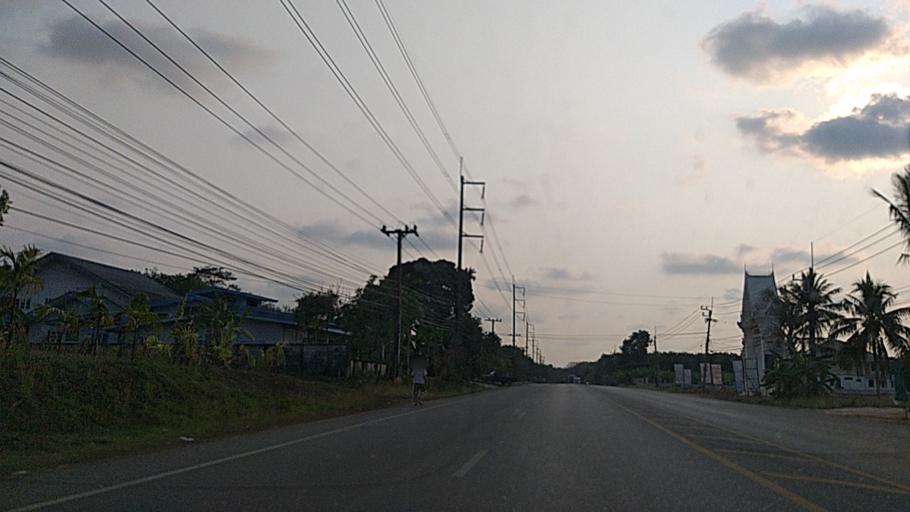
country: TH
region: Trat
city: Khao Saming
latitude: 12.3010
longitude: 102.3430
